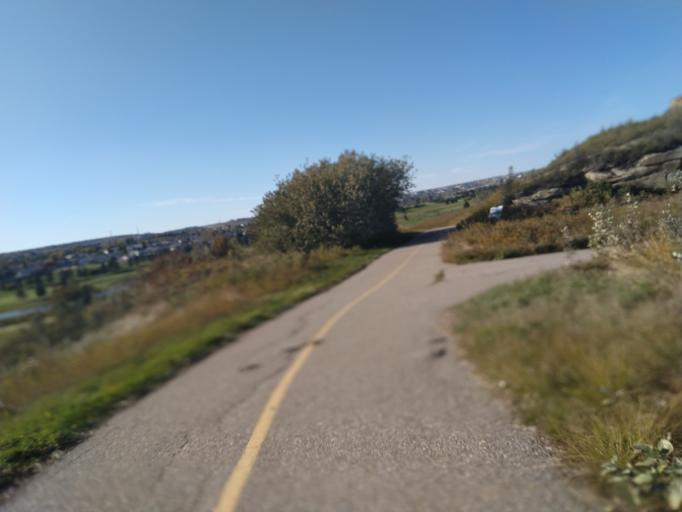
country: CA
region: Alberta
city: Calgary
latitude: 51.1473
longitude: -114.0894
